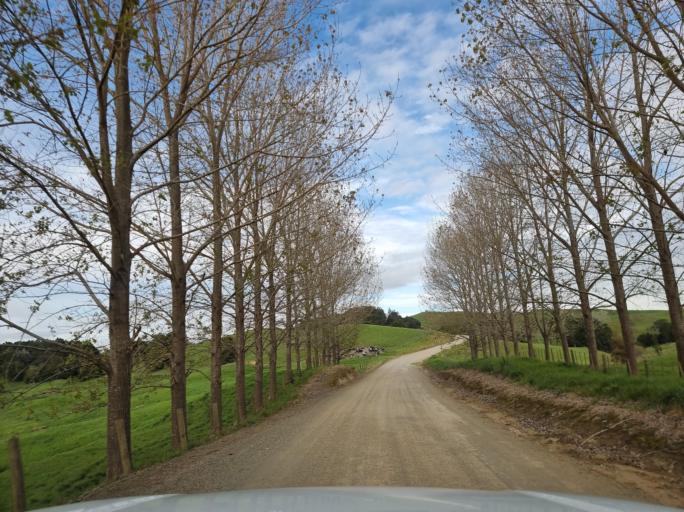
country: NZ
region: Northland
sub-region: Whangarei
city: Ruakaka
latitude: -36.0788
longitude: 174.3732
